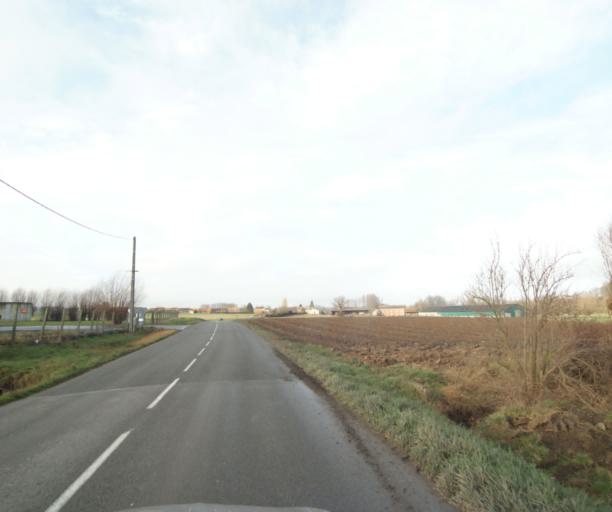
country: FR
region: Nord-Pas-de-Calais
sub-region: Departement du Nord
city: Vendegies-sur-Ecaillon
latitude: 50.2632
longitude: 3.4874
